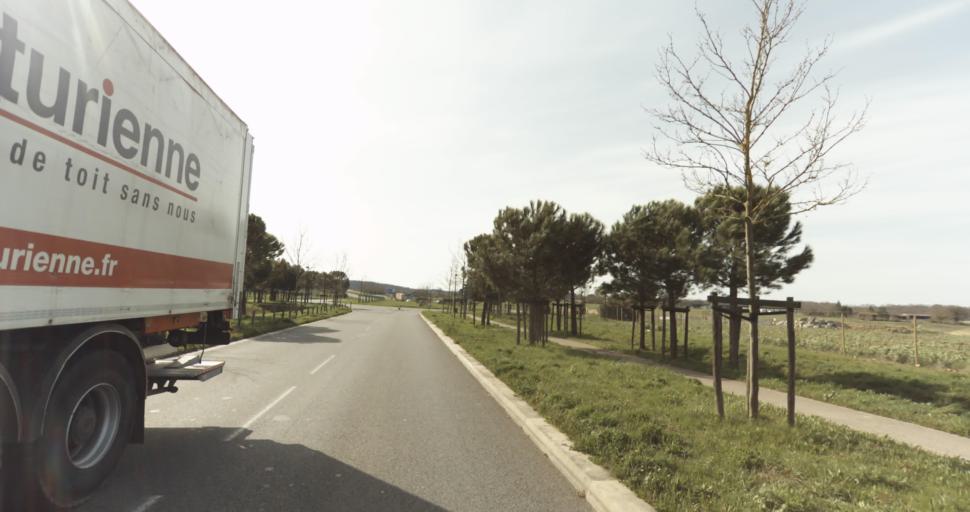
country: FR
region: Midi-Pyrenees
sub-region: Departement du Tarn
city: Saint-Sulpice-la-Pointe
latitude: 43.7584
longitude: 1.6586
